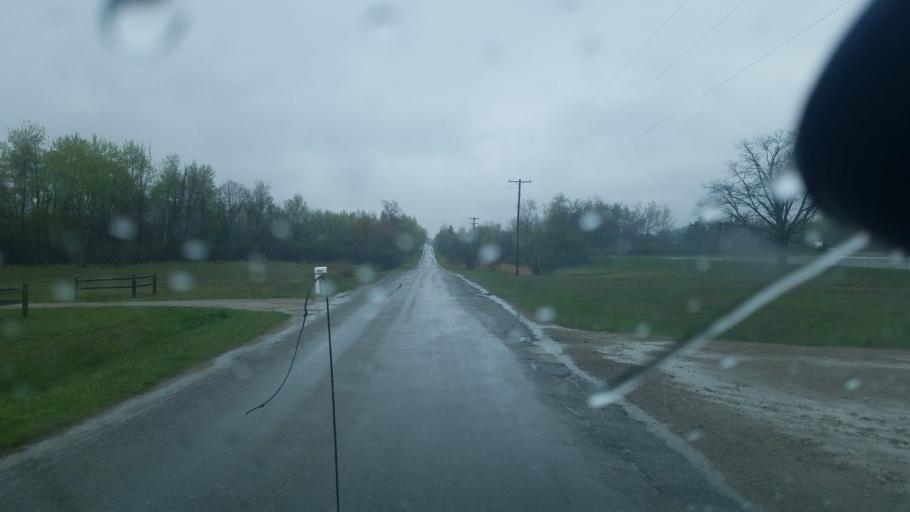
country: US
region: Michigan
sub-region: Montcalm County
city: Lakeview
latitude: 43.4485
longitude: -85.2933
